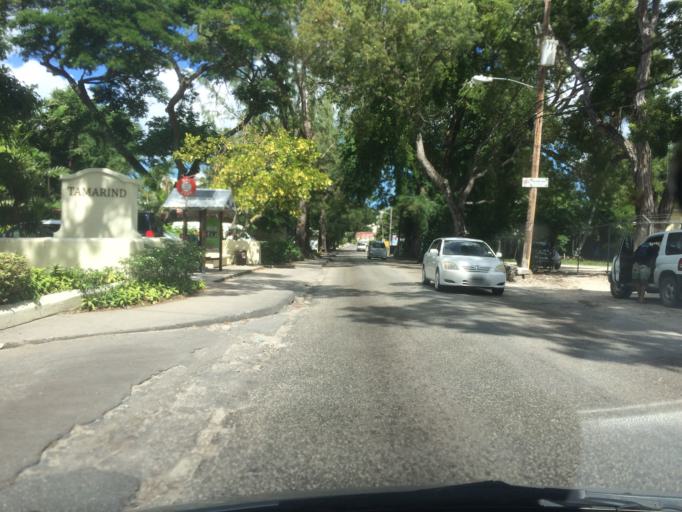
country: BB
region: Saint James
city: Holetown
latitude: 13.1630
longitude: -59.6368
